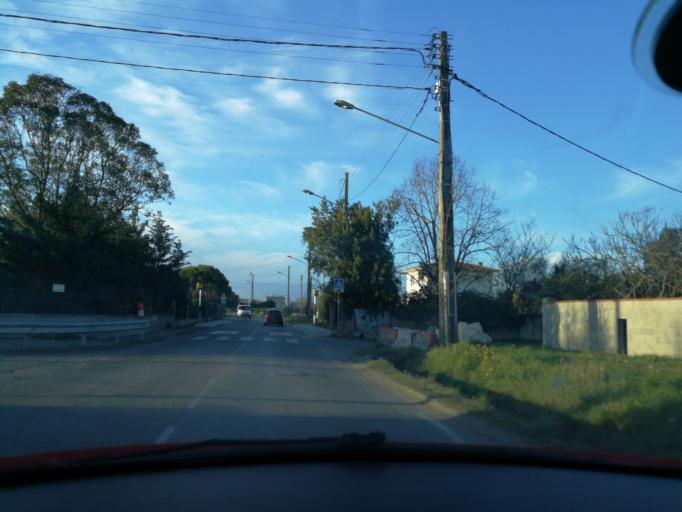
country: FR
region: Midi-Pyrenees
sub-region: Departement de la Haute-Garonne
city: Aucamville
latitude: 43.6500
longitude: 1.4136
